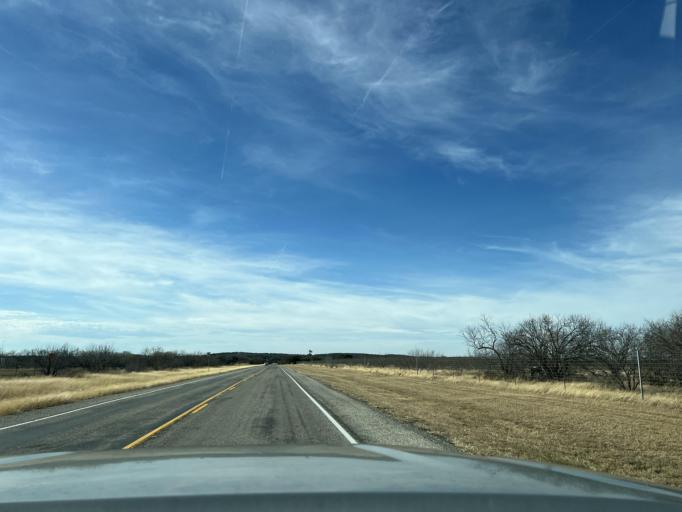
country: US
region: Texas
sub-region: Eastland County
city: Cisco
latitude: 32.4596
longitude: -98.9966
